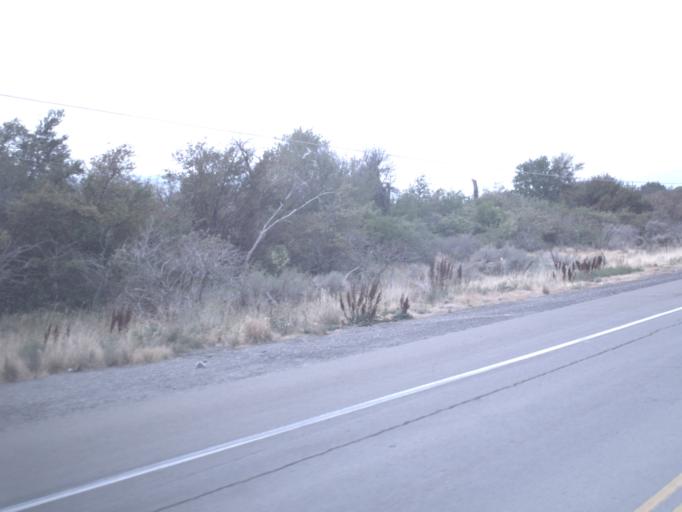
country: US
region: Utah
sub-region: Utah County
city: Cedar Hills
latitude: 40.4321
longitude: -111.7640
